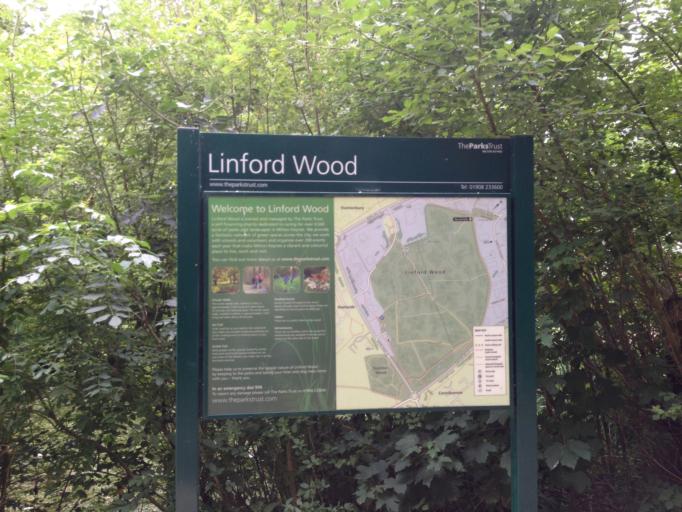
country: GB
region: England
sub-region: Milton Keynes
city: Milton Keynes
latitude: 52.0587
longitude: -0.7618
